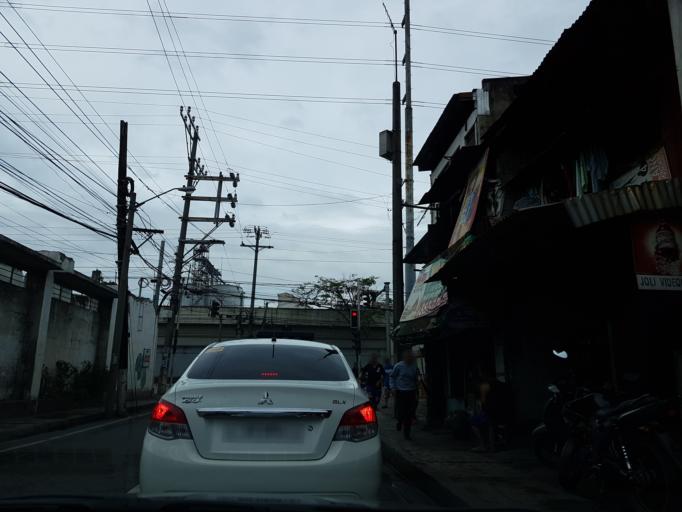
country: PH
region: Metro Manila
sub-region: Caloocan City
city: Niugan
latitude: 14.6715
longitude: 120.9822
